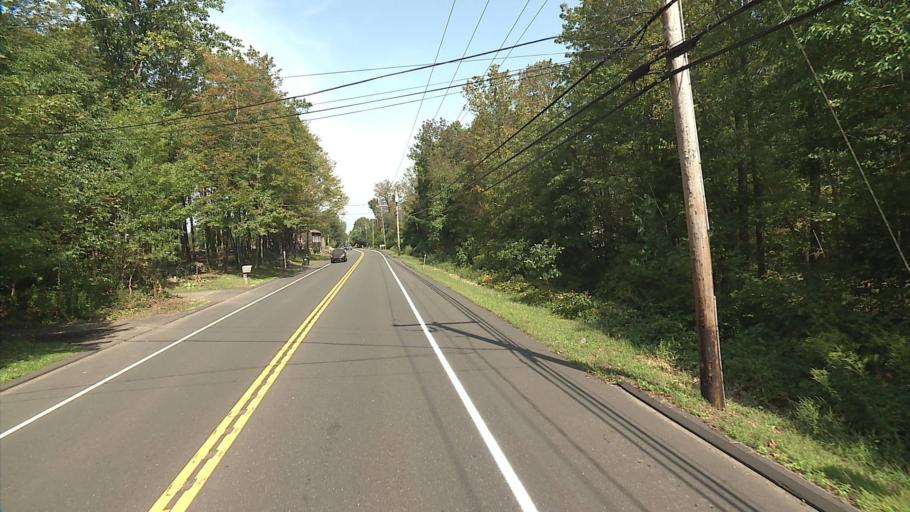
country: US
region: Connecticut
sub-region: New Haven County
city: Guilford
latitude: 41.3717
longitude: -72.6391
